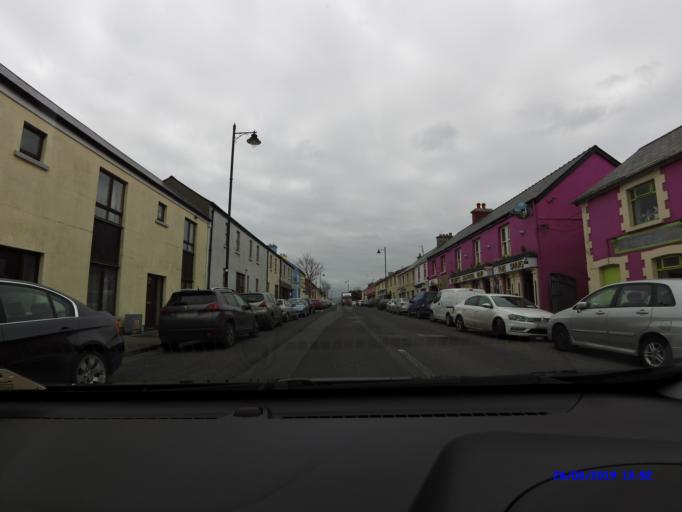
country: IE
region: Connaught
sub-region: Maigh Eo
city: Belmullet
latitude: 54.2234
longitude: -9.9858
